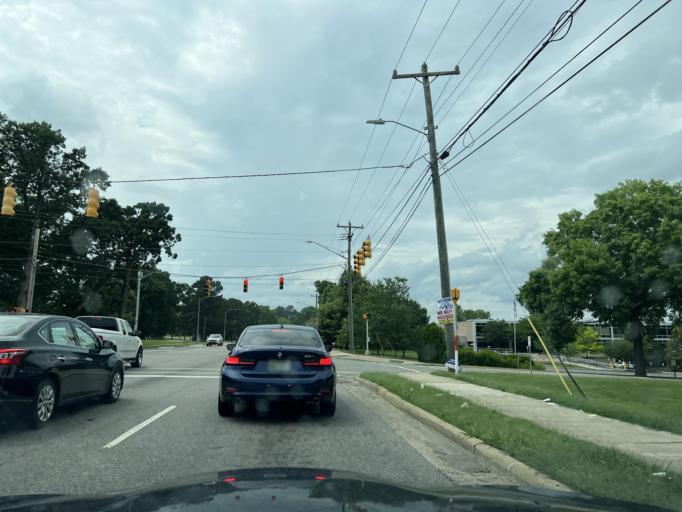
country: US
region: North Carolina
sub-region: Durham County
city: Durham
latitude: 36.0371
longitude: -78.8964
